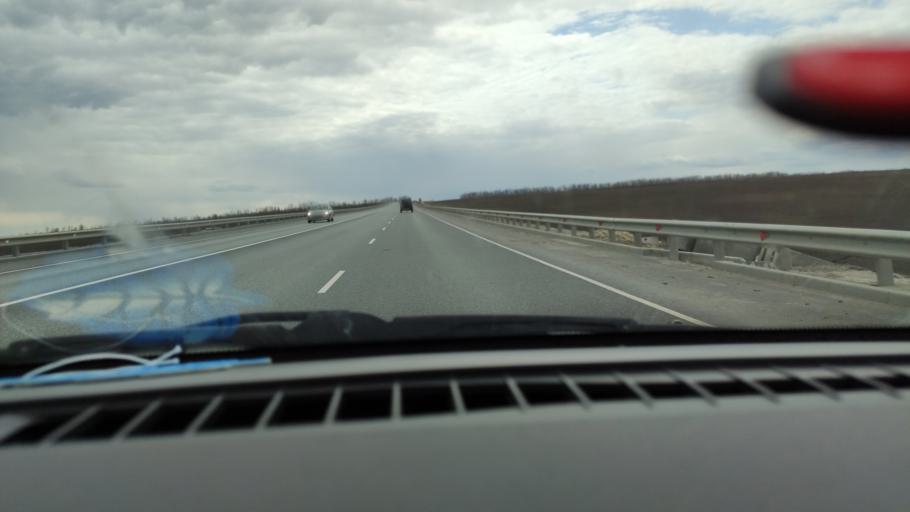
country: RU
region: Saratov
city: Yelshanka
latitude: 51.8366
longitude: 46.4736
